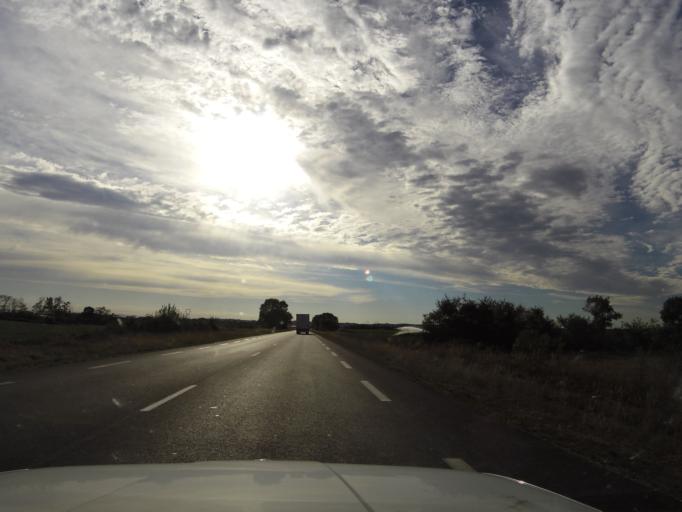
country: FR
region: Rhone-Alpes
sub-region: Departement de l'Ain
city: Saint-Jean-de-Niost
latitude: 45.8589
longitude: 5.1957
